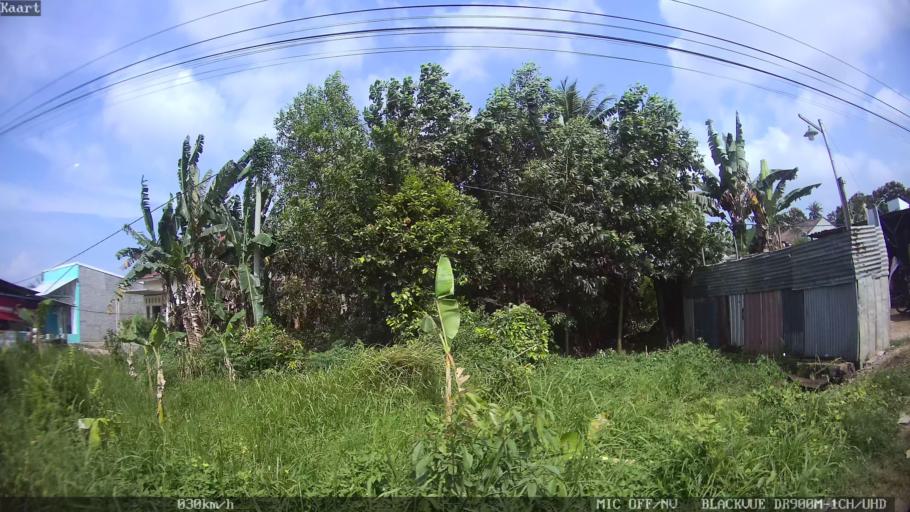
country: ID
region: Lampung
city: Kedaton
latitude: -5.3301
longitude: 105.2825
